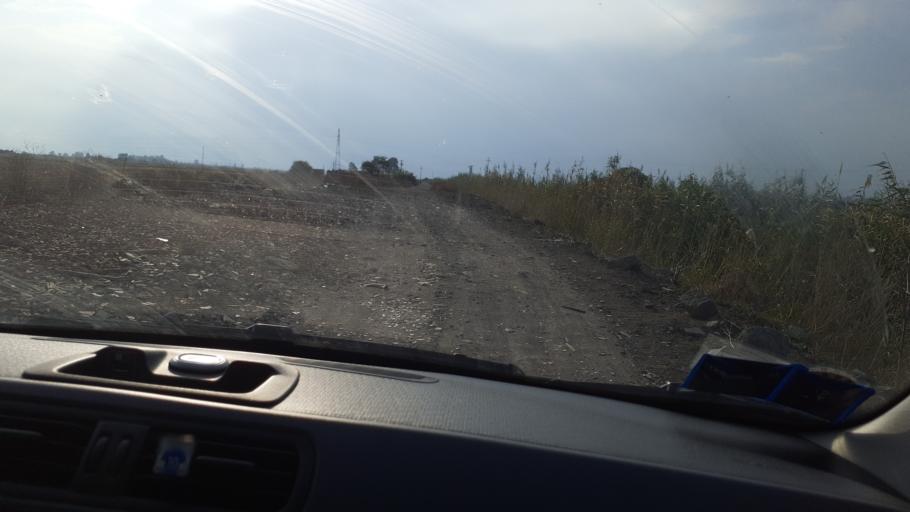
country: IT
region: Sicily
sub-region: Catania
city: Catania
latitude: 37.4333
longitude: 15.0105
